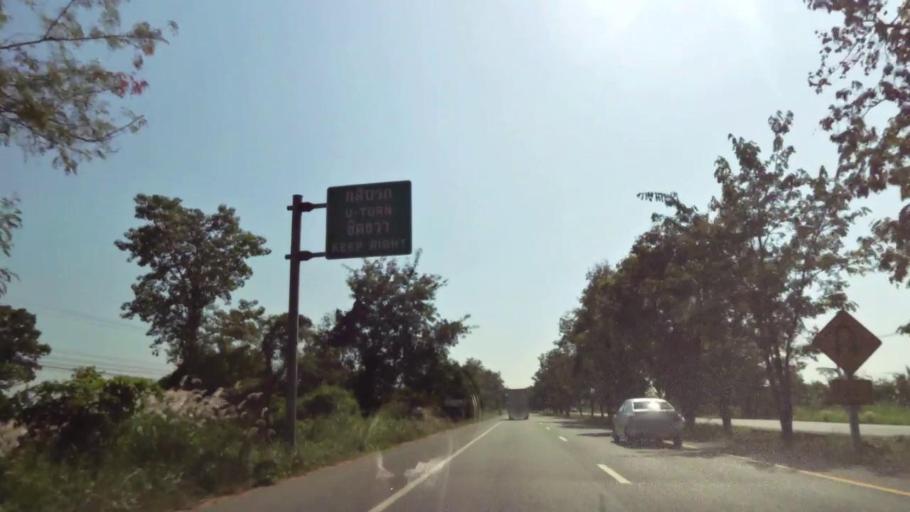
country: TH
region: Nakhon Sawan
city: Kao Liao
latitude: 15.9074
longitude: 100.1125
